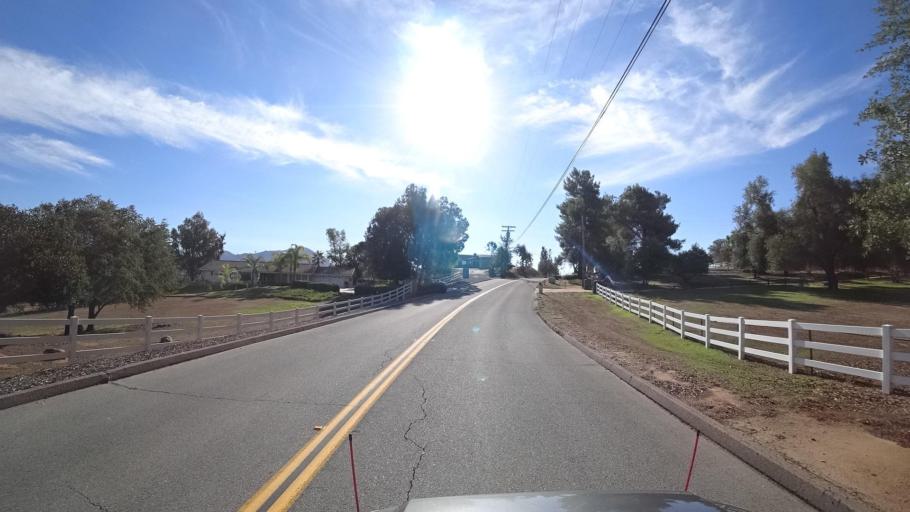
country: US
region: California
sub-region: San Diego County
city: Alpine
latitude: 32.8187
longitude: -116.7501
